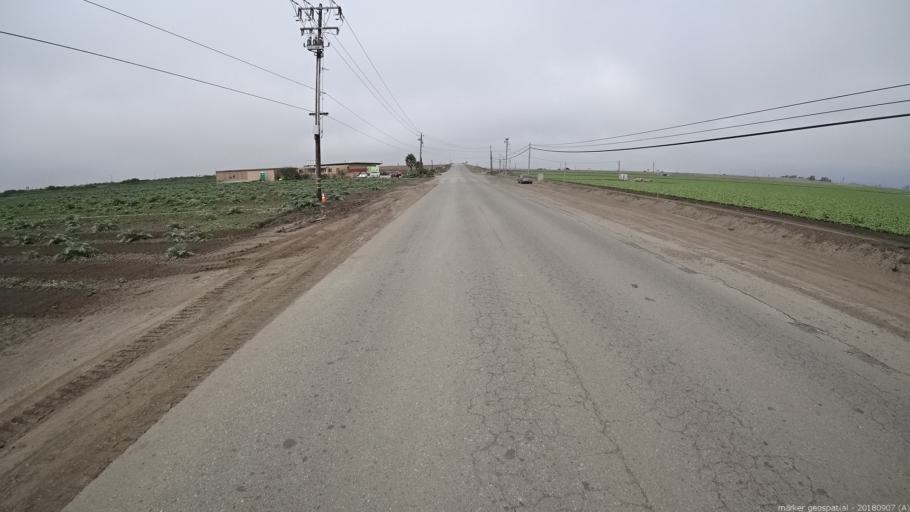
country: US
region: California
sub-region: Monterey County
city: Castroville
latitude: 36.7424
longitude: -121.7676
